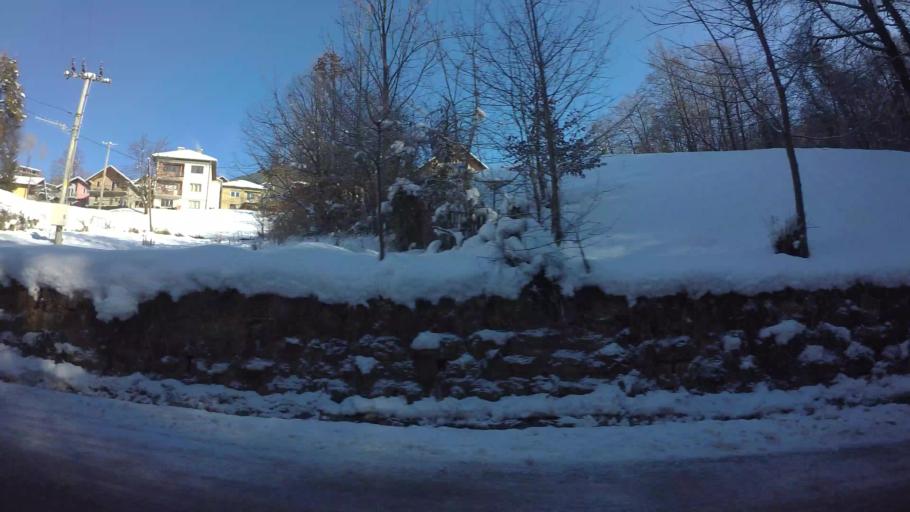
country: BA
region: Federation of Bosnia and Herzegovina
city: Kobilja Glava
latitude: 43.8915
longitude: 18.4179
